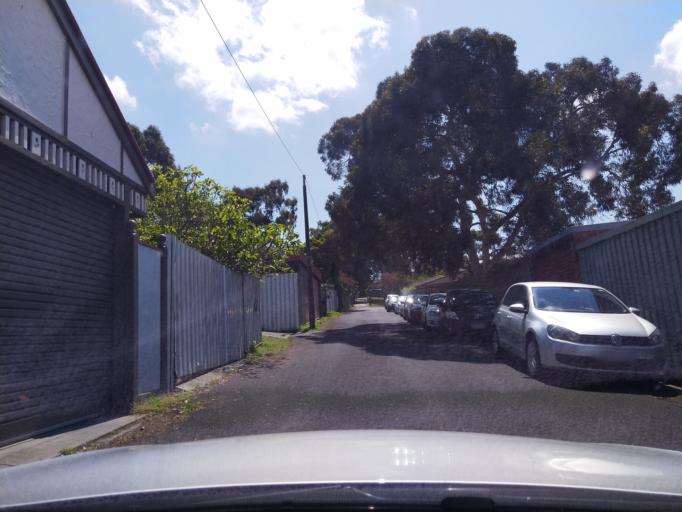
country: AU
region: Victoria
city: Rosanna
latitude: -37.7606
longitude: 145.0554
